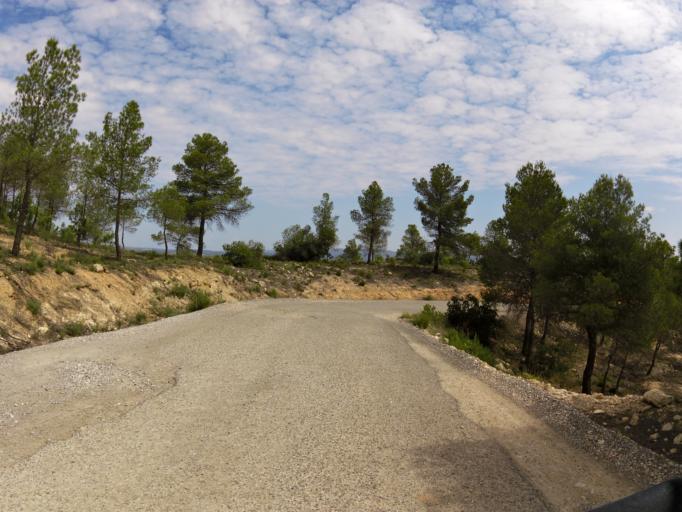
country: ES
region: Castille-La Mancha
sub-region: Provincia de Albacete
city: Casas Ibanez
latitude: 39.3612
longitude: -1.4710
